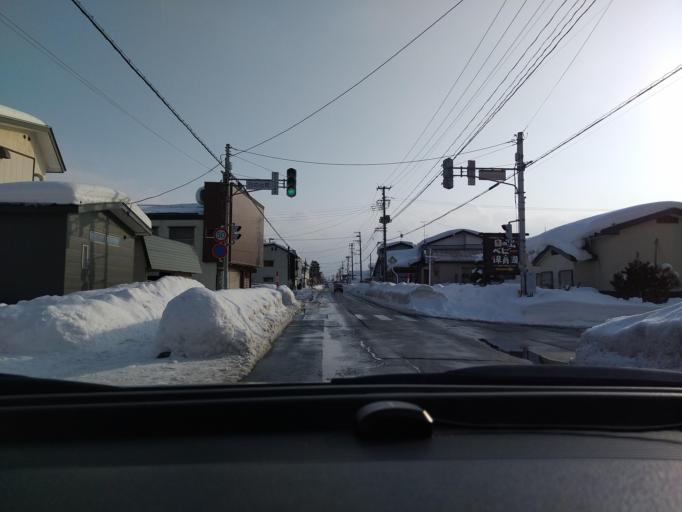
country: JP
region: Akita
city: Omagari
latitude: 39.4461
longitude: 140.4799
